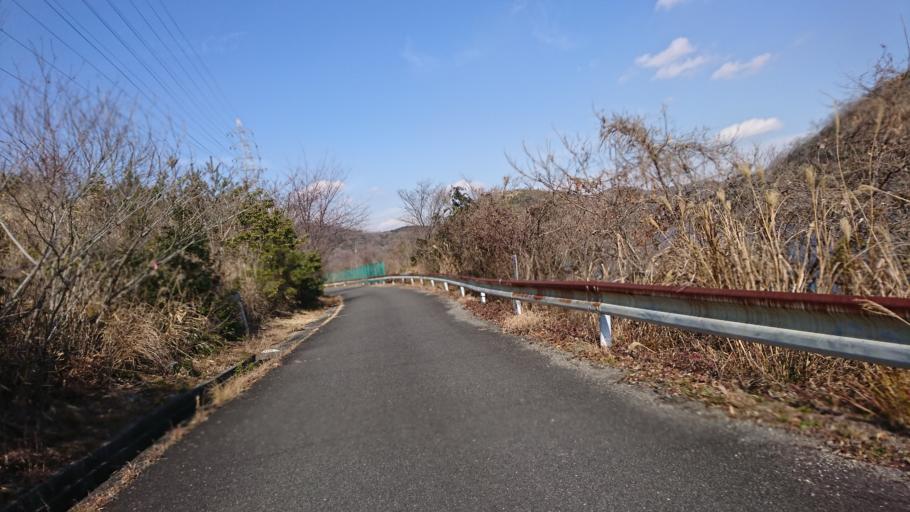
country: JP
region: Hyogo
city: Ono
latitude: 34.8289
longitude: 134.8733
